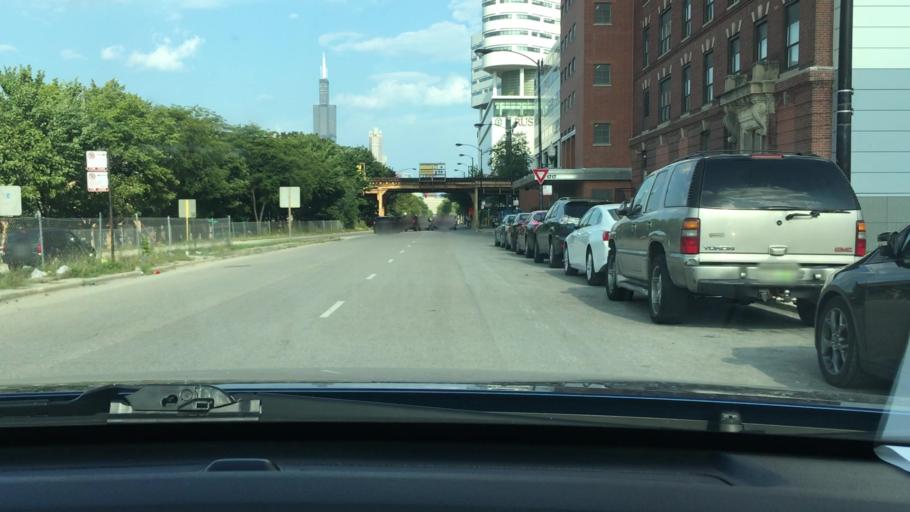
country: US
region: Illinois
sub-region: Cook County
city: Chicago
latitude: 41.8751
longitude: -87.6711
